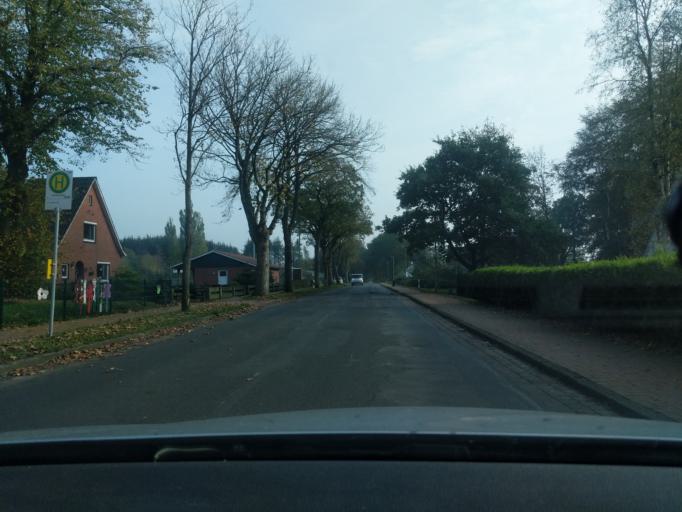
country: DE
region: Lower Saxony
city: Stinstedt
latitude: 53.6599
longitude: 8.9733
